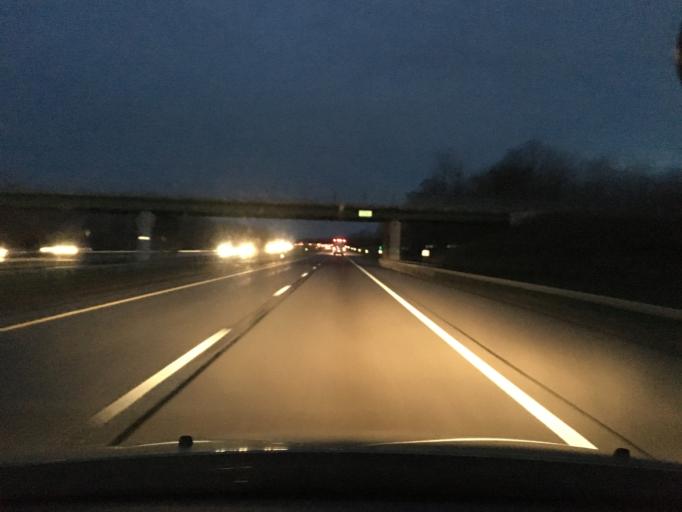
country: US
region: New York
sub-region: Ontario County
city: Manchester
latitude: 42.9812
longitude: -77.2778
